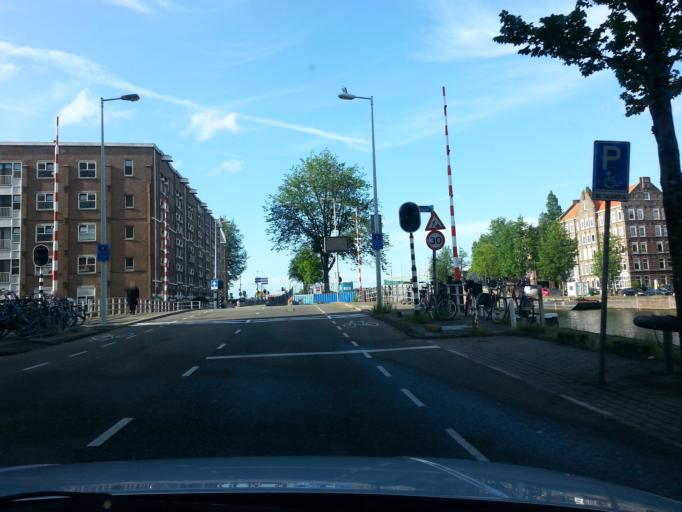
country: NL
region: North Holland
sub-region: Gemeente Amsterdam
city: Amsterdam
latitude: 52.3890
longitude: 4.8845
